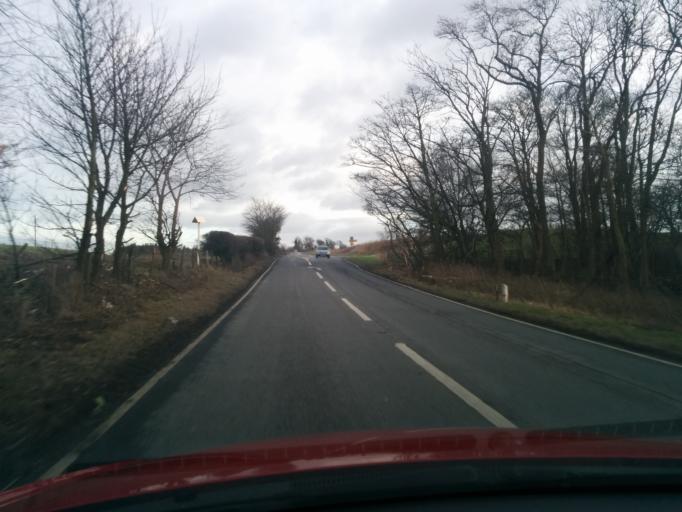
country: GB
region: Scotland
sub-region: Fife
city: Limekilns
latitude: 55.9838
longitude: -3.5120
